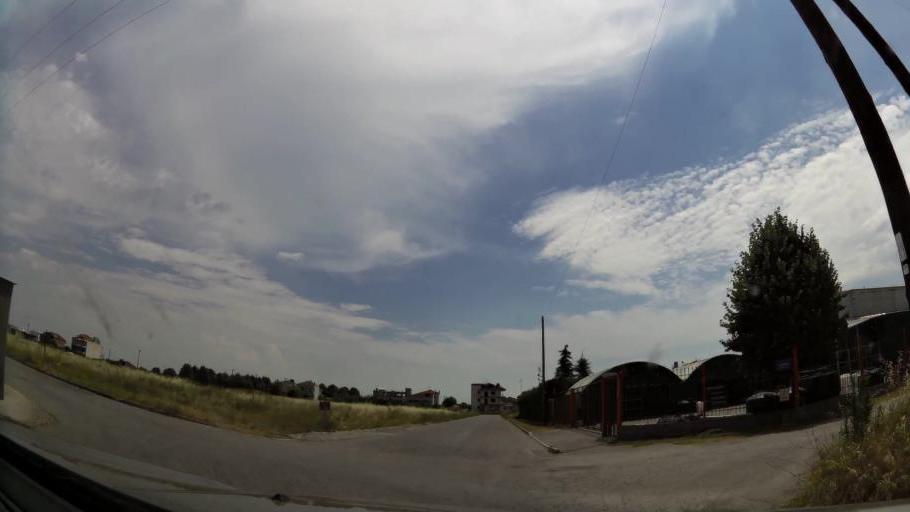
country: GR
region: Central Macedonia
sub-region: Nomos Pierias
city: Katerini
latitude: 40.2592
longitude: 22.5128
